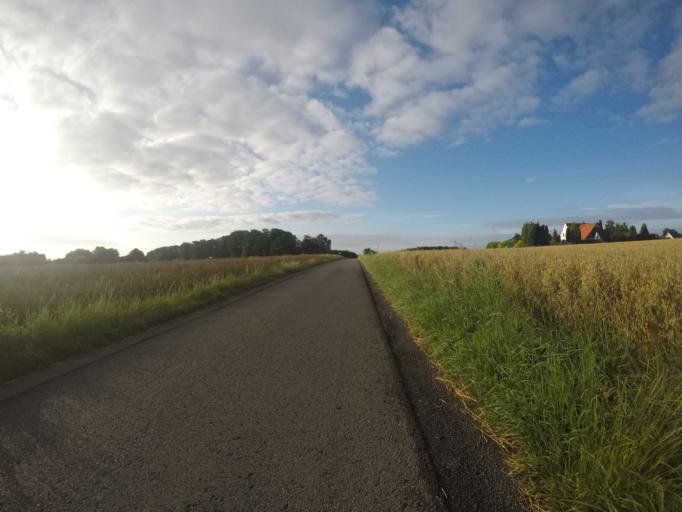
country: DE
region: North Rhine-Westphalia
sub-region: Regierungsbezirk Detmold
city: Herford
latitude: 52.0968
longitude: 8.6182
